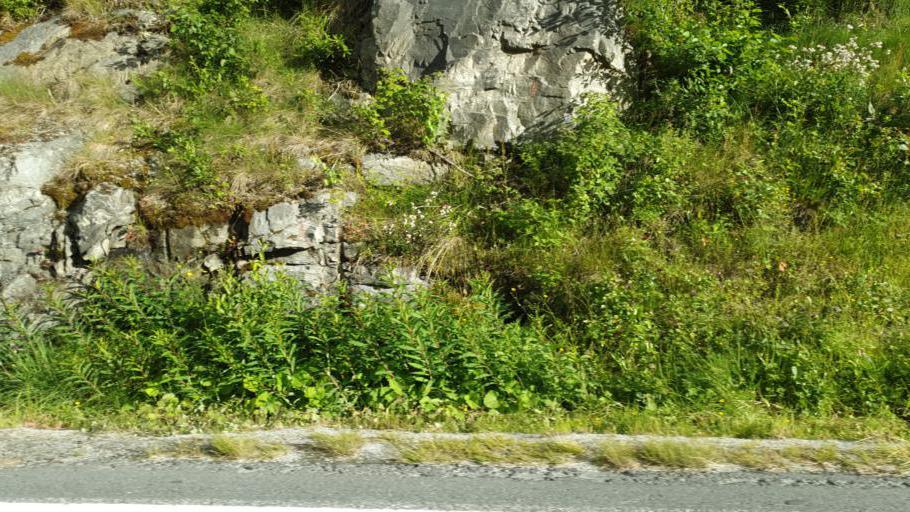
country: NO
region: Oppland
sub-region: Vaga
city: Vagamo
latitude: 61.8473
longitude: 8.9893
